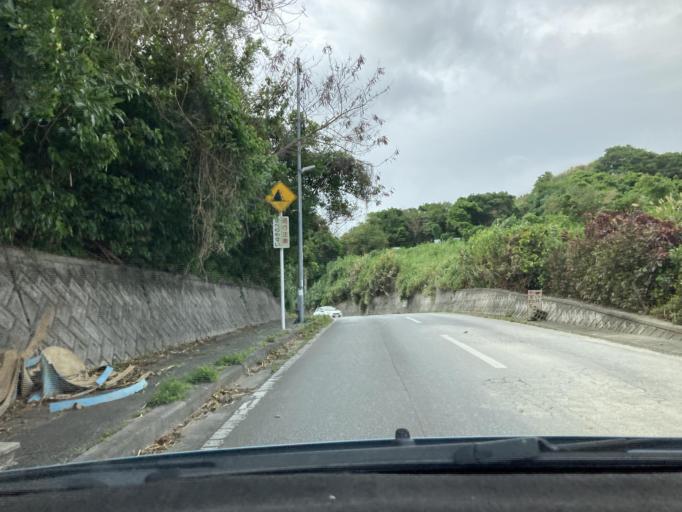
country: JP
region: Okinawa
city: Ginowan
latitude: 26.2302
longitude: 127.7438
